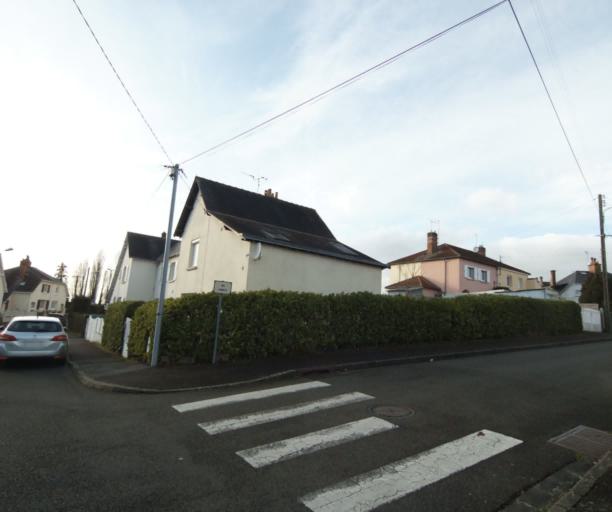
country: FR
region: Pays de la Loire
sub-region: Departement de la Sarthe
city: Le Mans
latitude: 47.9638
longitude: 0.2026
